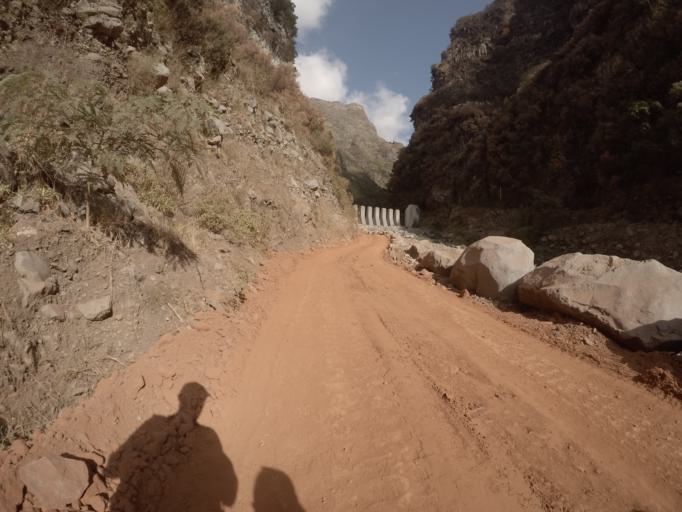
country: PT
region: Madeira
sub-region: Funchal
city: Nossa Senhora do Monte
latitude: 32.6960
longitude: -16.9182
